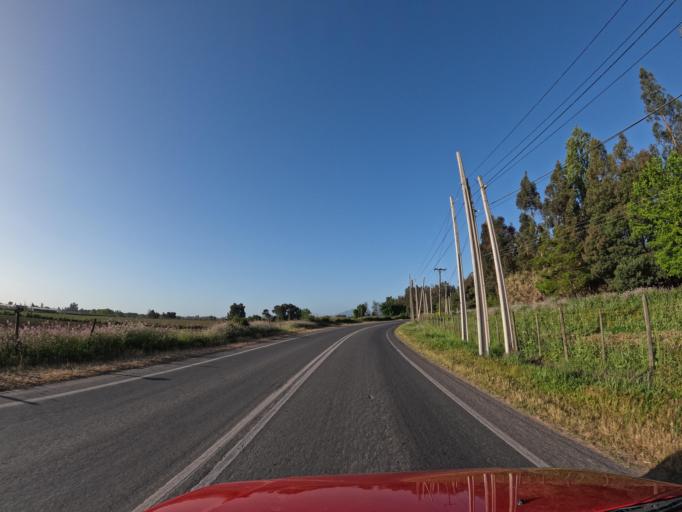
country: CL
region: O'Higgins
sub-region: Provincia de Colchagua
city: Santa Cruz
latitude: -34.5262
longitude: -71.3855
